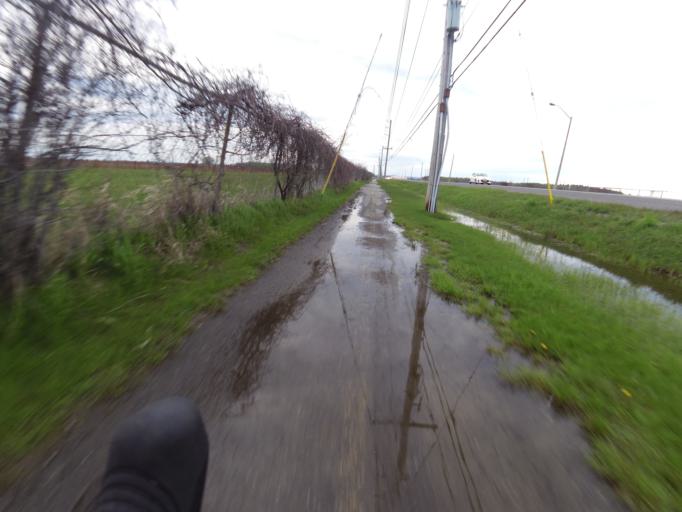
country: CA
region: Ontario
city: Bells Corners
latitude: 45.3035
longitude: -75.7664
